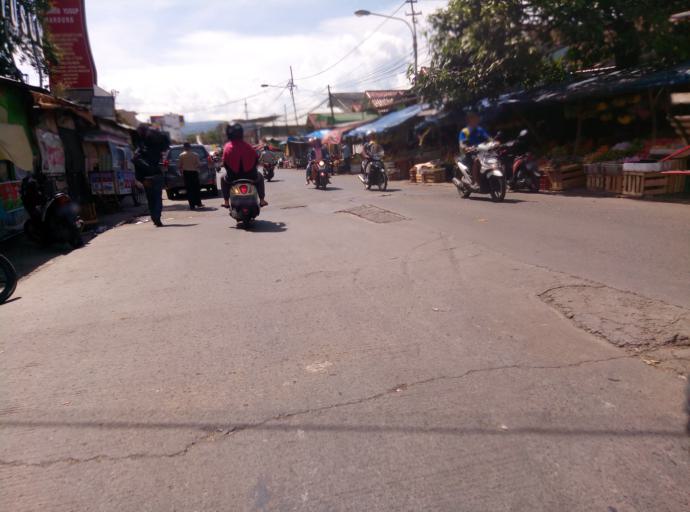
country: ID
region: West Java
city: Bandung
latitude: -6.9072
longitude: 107.6438
